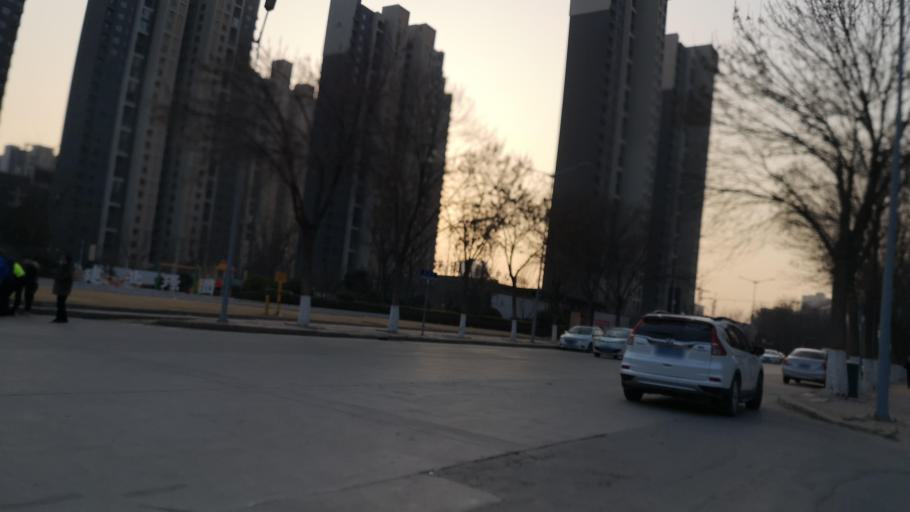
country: CN
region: Henan Sheng
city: Zhongyuanlu
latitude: 35.7235
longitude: 115.0558
